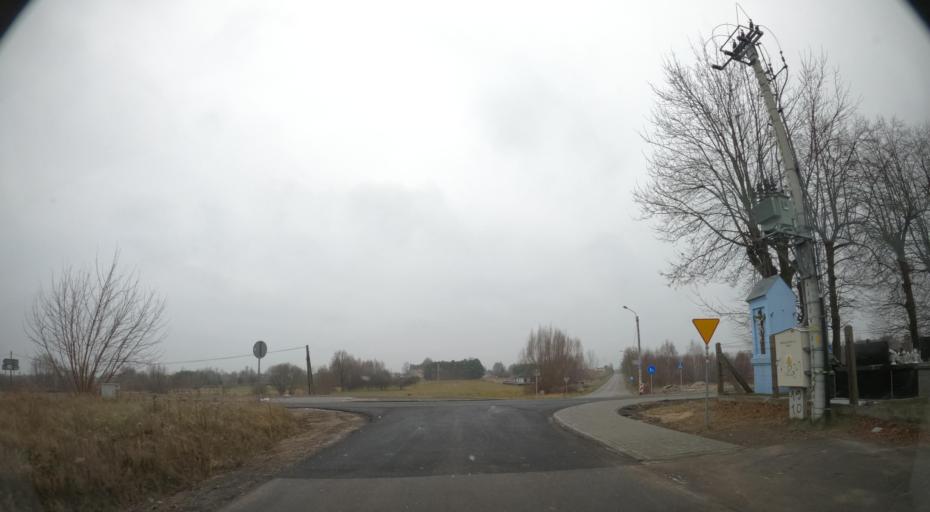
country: PL
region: Masovian Voivodeship
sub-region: Powiat radomski
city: Skaryszew
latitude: 51.3908
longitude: 21.2622
